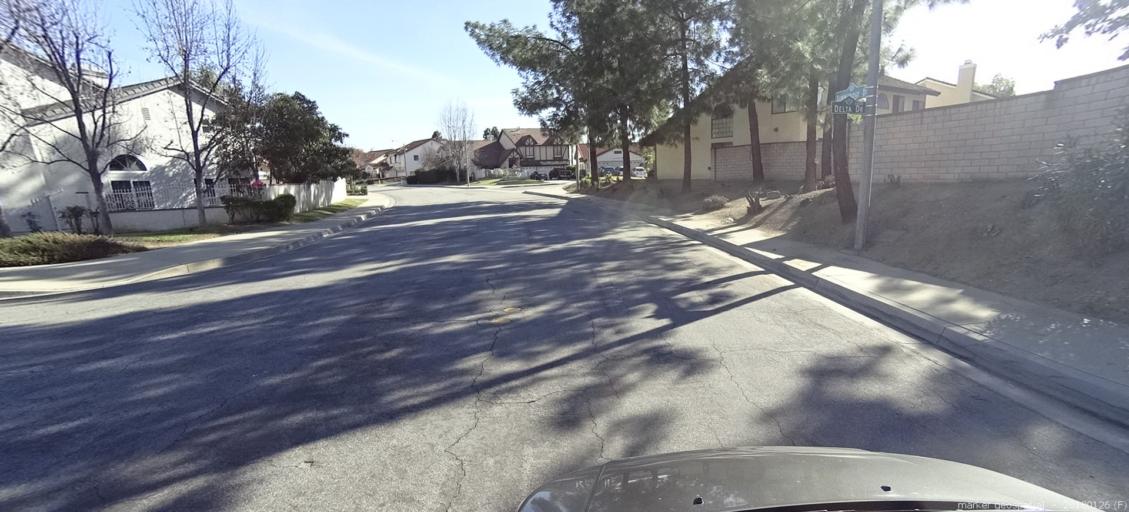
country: US
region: California
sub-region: Los Angeles County
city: Diamond Bar
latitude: 33.9953
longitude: -117.7980
